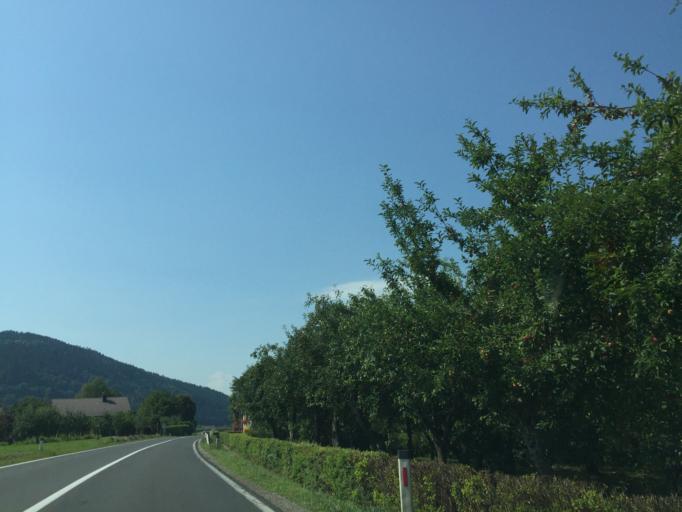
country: SI
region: Slovenj Gradec
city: Pamece
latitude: 46.5424
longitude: 15.0614
